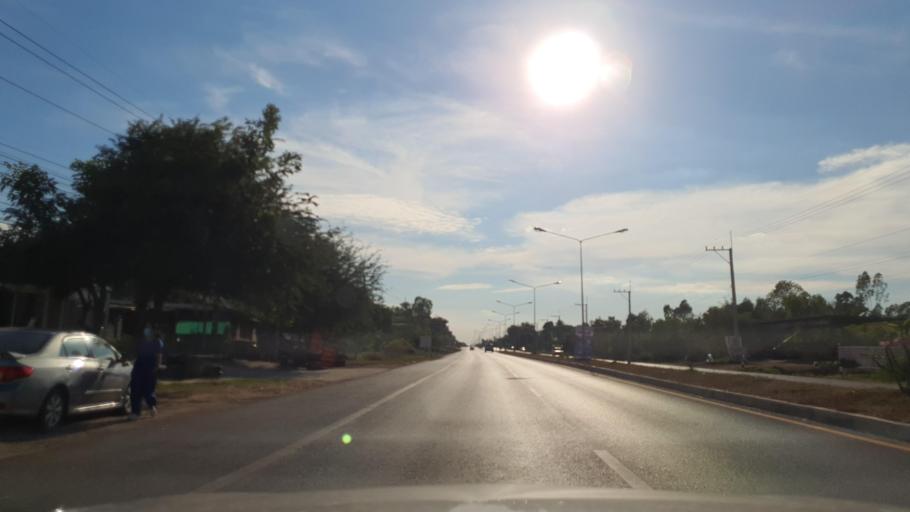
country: TH
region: Maha Sarakham
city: Kantharawichai
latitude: 16.3496
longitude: 103.3250
